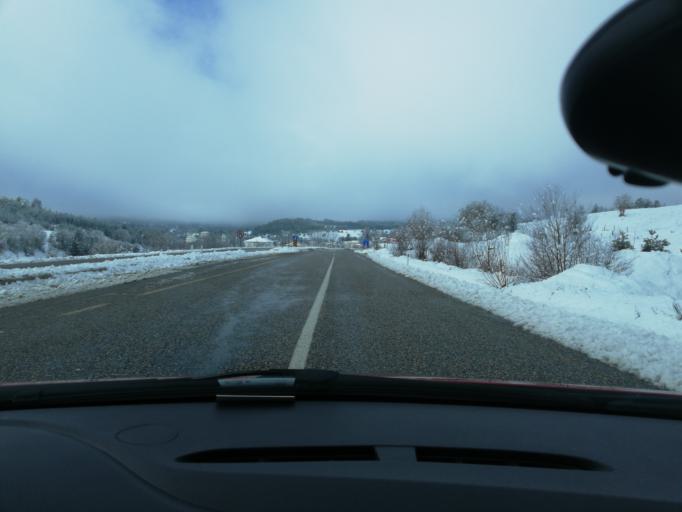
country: TR
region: Kastamonu
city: Ihsangazi
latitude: 41.3047
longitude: 33.5501
